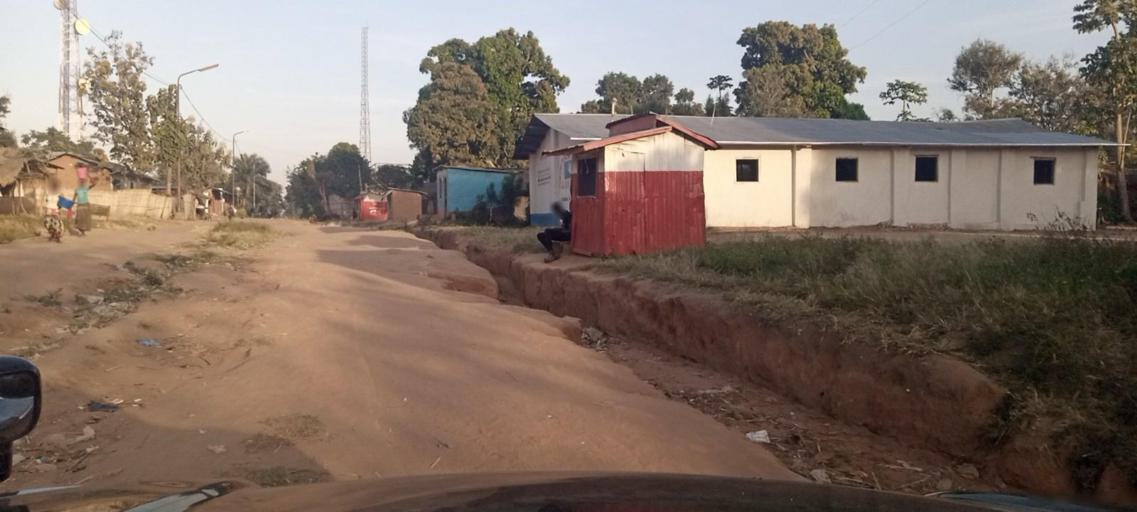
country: CD
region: Kasai-Oriental
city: Lubao
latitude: -5.3845
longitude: 25.7478
